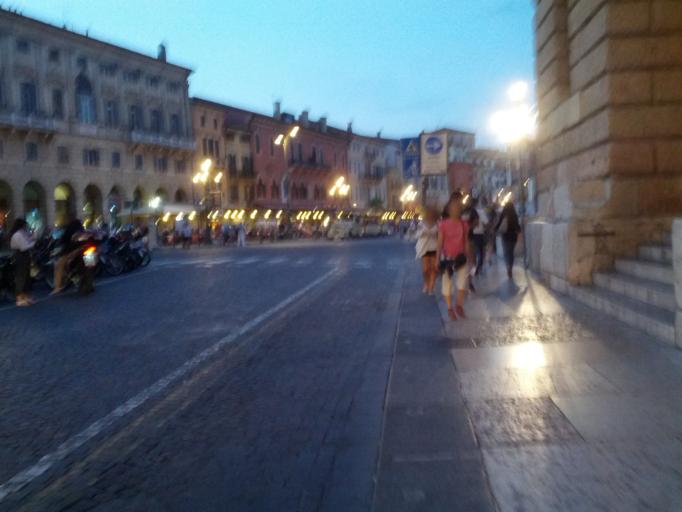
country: IT
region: Veneto
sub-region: Provincia di Verona
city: Verona
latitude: 45.4380
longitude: 10.9916
